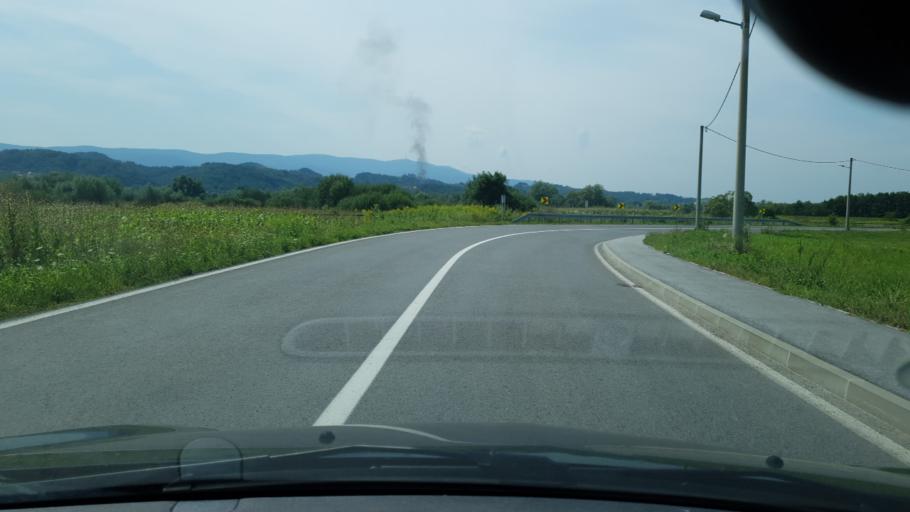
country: HR
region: Krapinsko-Zagorska
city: Bedekovcina
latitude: 46.0238
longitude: 15.9590
